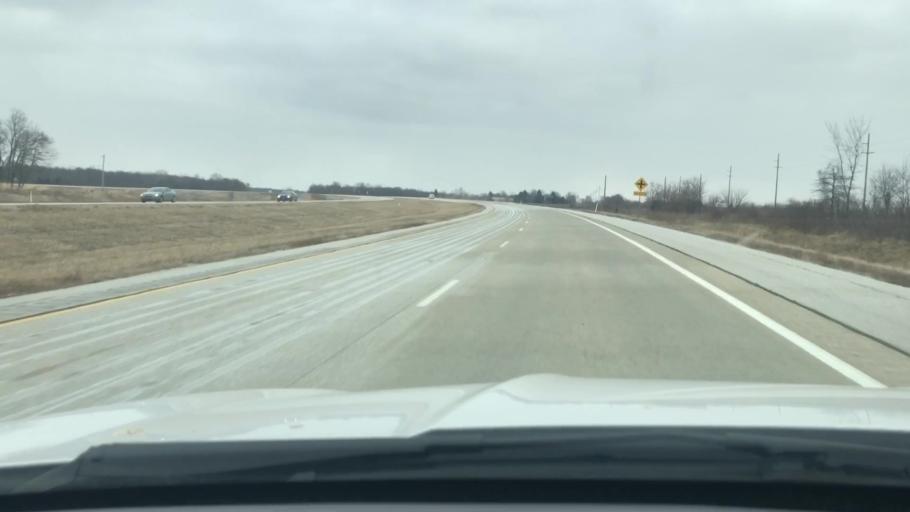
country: US
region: Indiana
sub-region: Tippecanoe County
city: Battle Ground
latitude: 40.4802
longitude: -86.7796
